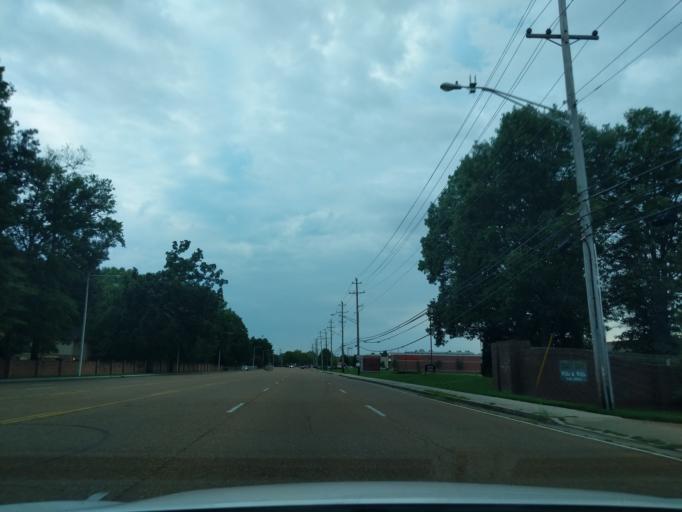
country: US
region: Tennessee
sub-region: Shelby County
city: Germantown
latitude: 35.0752
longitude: -89.8424
